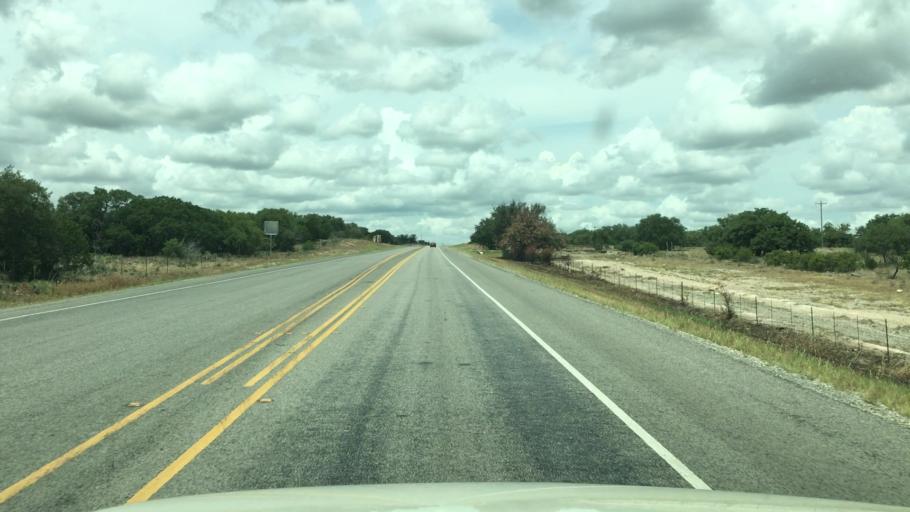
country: US
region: Texas
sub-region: McCulloch County
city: Brady
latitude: 31.0307
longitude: -99.2298
